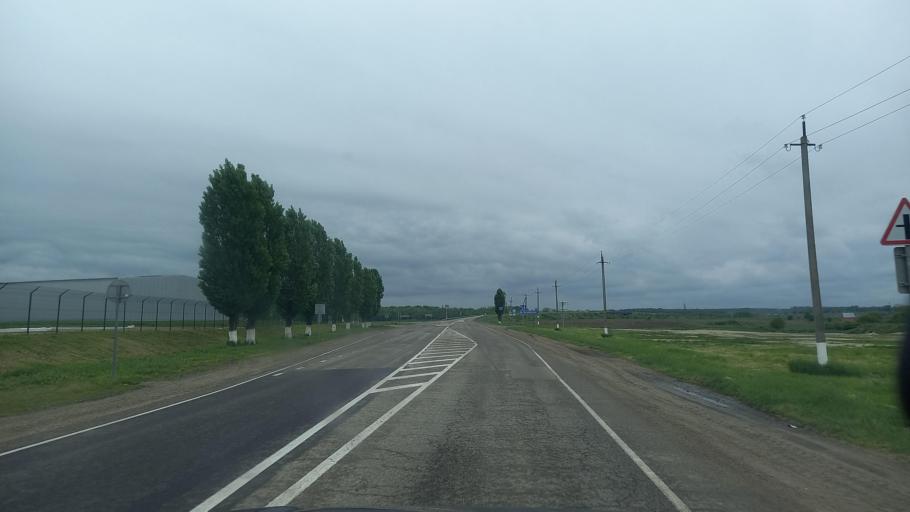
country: RU
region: Krasnodarskiy
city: Konokovo
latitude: 44.8447
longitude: 41.3500
